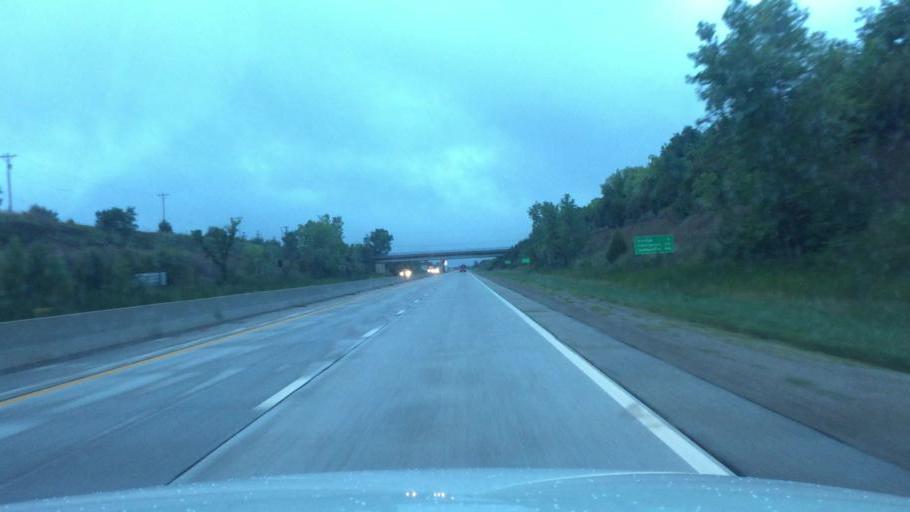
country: US
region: Kansas
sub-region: Neosho County
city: Chanute
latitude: 37.6779
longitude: -95.4796
